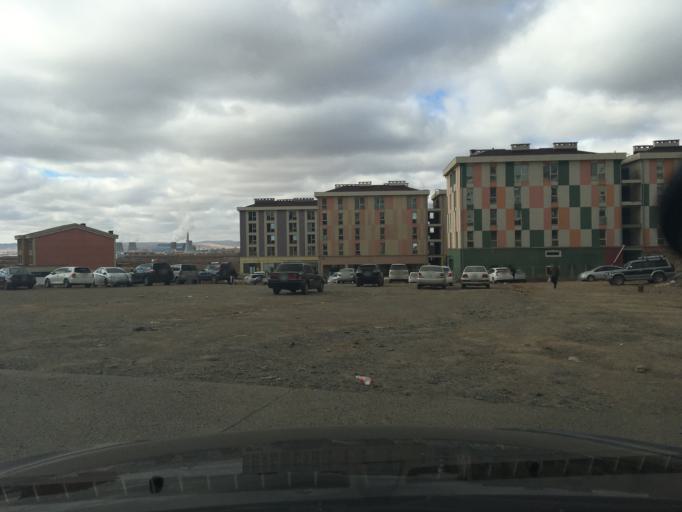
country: MN
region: Ulaanbaatar
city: Ulaanbaatar
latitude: 47.8797
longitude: 106.8517
